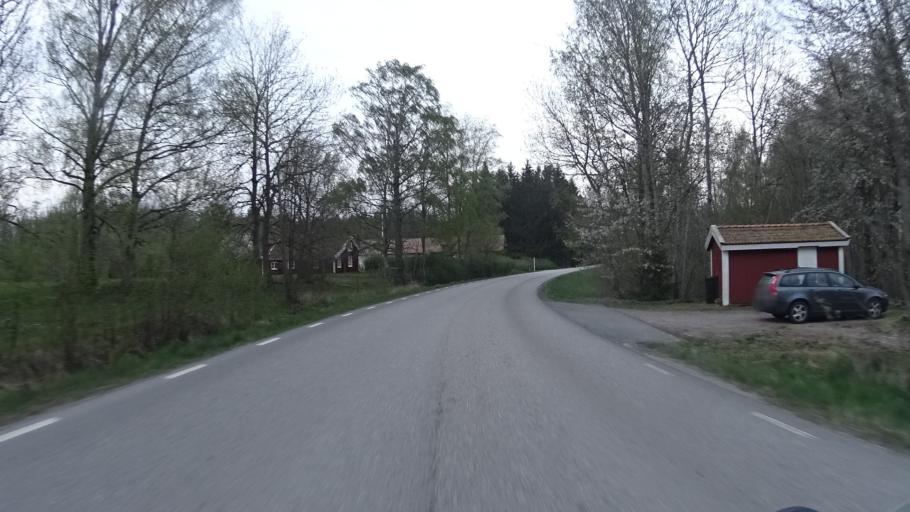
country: SE
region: Vaestra Goetaland
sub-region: Gotene Kommun
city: Kallby
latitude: 58.5304
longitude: 13.3247
